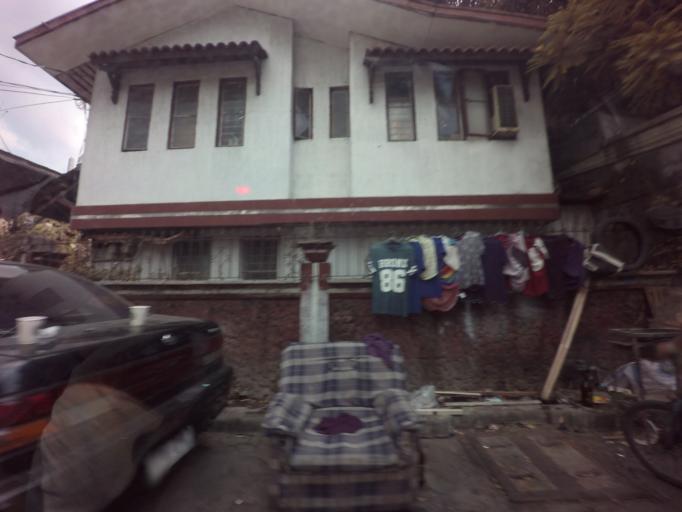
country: PH
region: Metro Manila
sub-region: Makati City
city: Makati City
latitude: 14.5692
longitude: 121.0205
